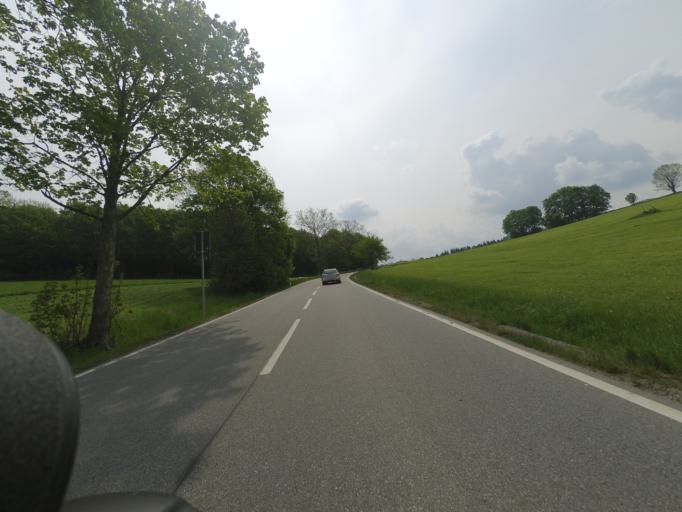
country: DE
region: Saxony
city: Olbernhau
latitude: 50.6529
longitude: 13.3054
